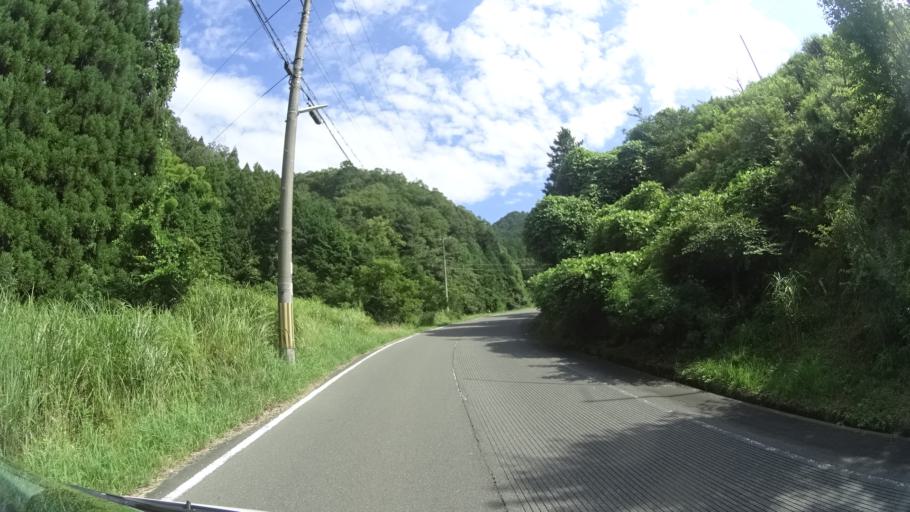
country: JP
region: Kyoto
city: Fukuchiyama
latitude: 35.3481
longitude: 135.1538
